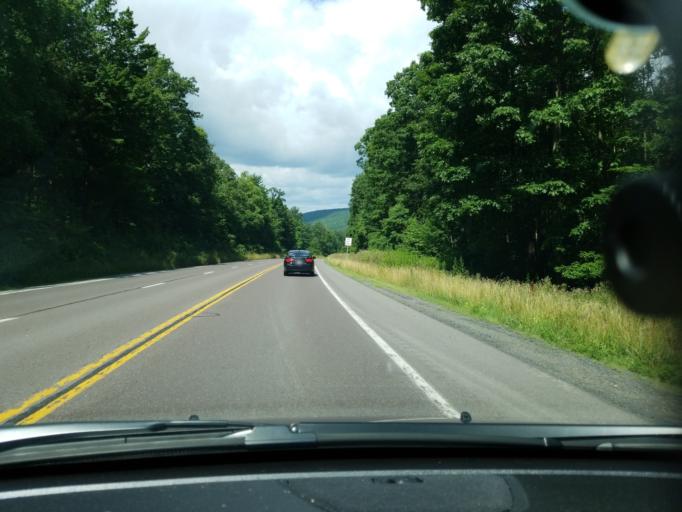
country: US
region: Pennsylvania
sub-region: Northumberland County
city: Kulpmont
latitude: 40.8205
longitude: -76.4860
